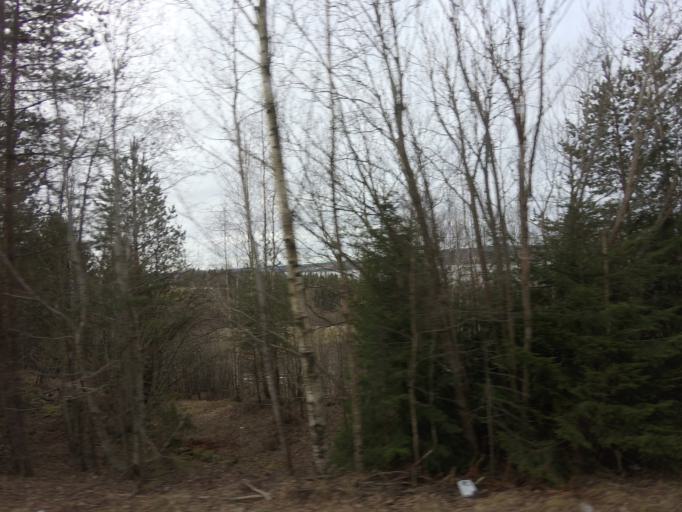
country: NO
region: Akershus
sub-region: Enebakk
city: Flateby
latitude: 59.8109
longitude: 11.2489
